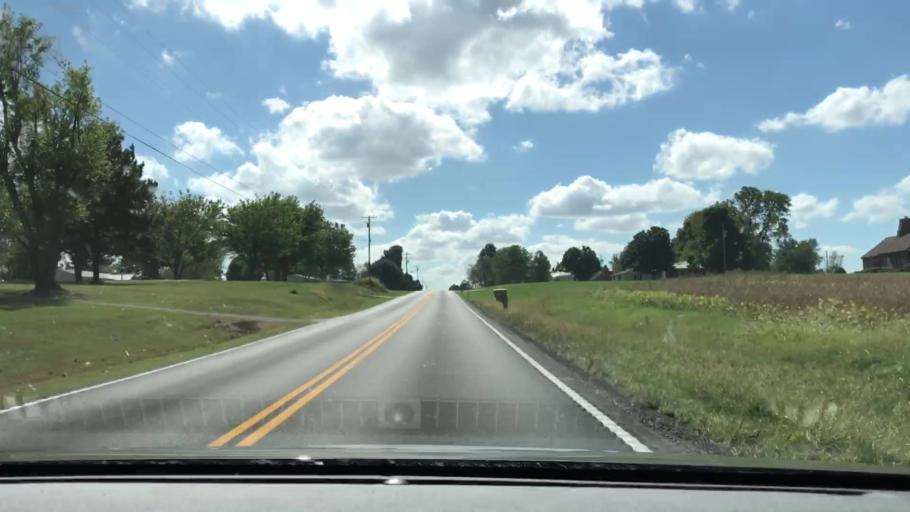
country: US
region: Kentucky
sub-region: Graves County
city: Mayfield
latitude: 36.8053
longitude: -88.5954
